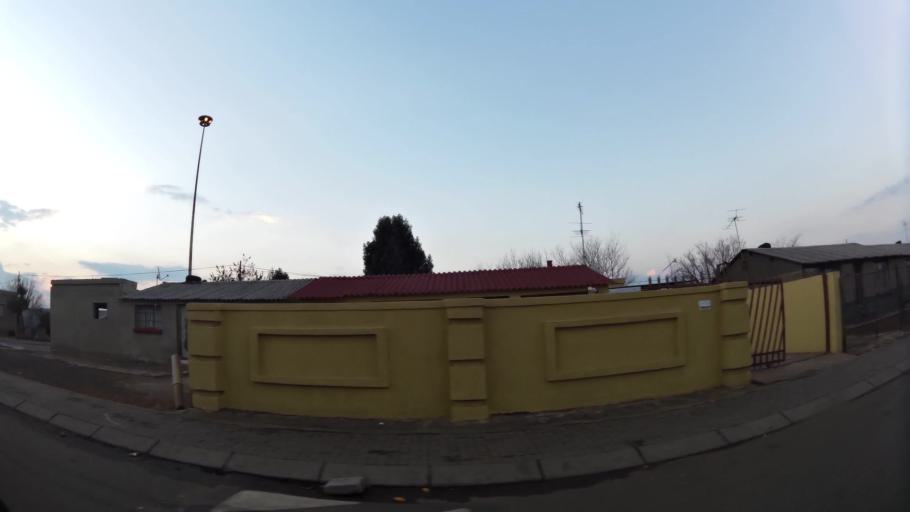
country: ZA
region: Gauteng
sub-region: City of Johannesburg Metropolitan Municipality
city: Orange Farm
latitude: -26.5580
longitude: 27.8653
